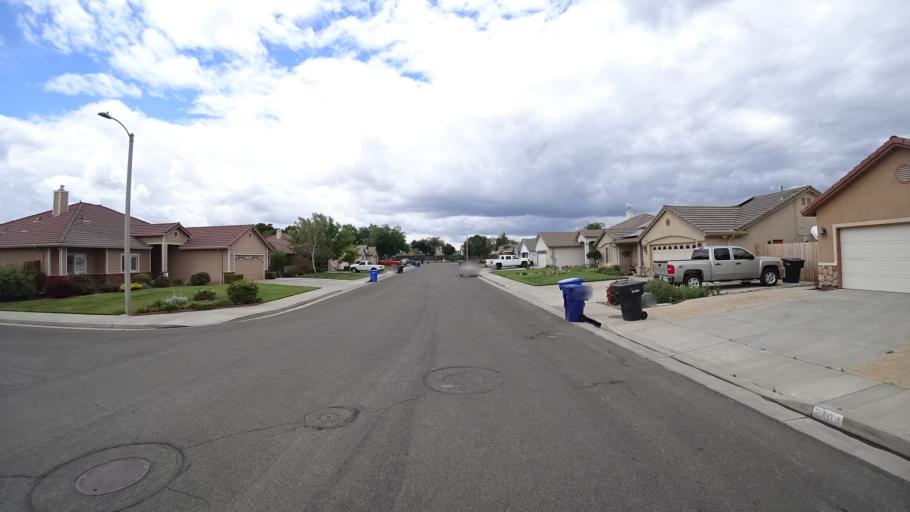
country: US
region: California
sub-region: Kings County
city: Armona
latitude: 36.3318
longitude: -119.6805
